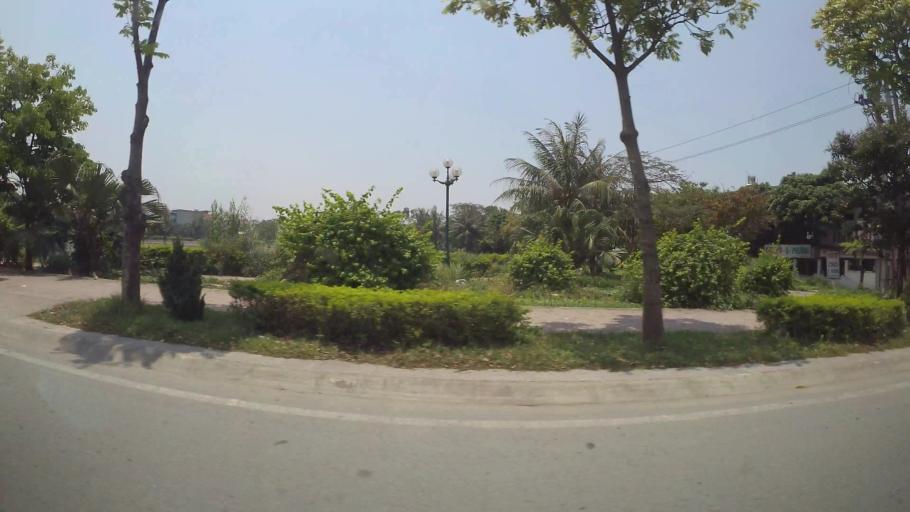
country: VN
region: Ha Noi
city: Trau Quy
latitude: 21.0294
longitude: 105.9127
